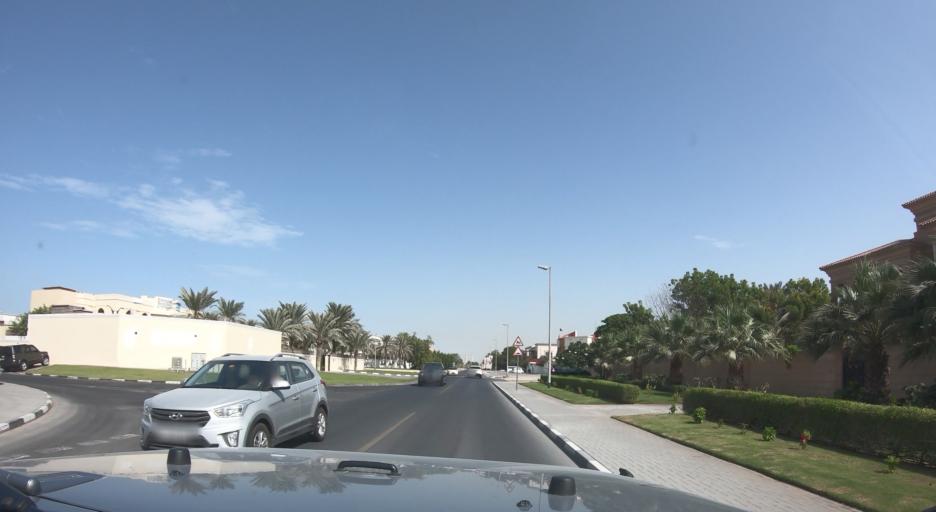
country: AE
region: Dubai
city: Dubai
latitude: 25.1596
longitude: 55.2240
